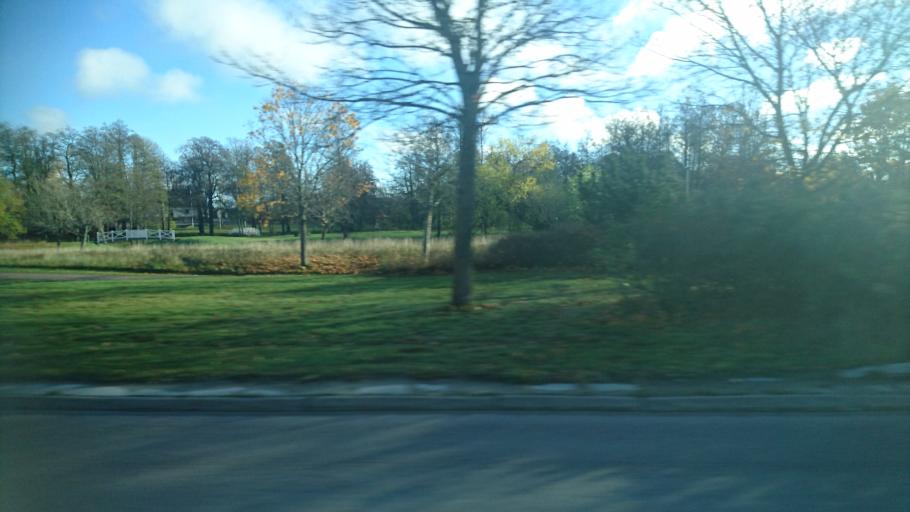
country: SE
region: Vaestmanland
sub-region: Sala Kommun
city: Sala
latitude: 59.9273
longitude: 16.5905
